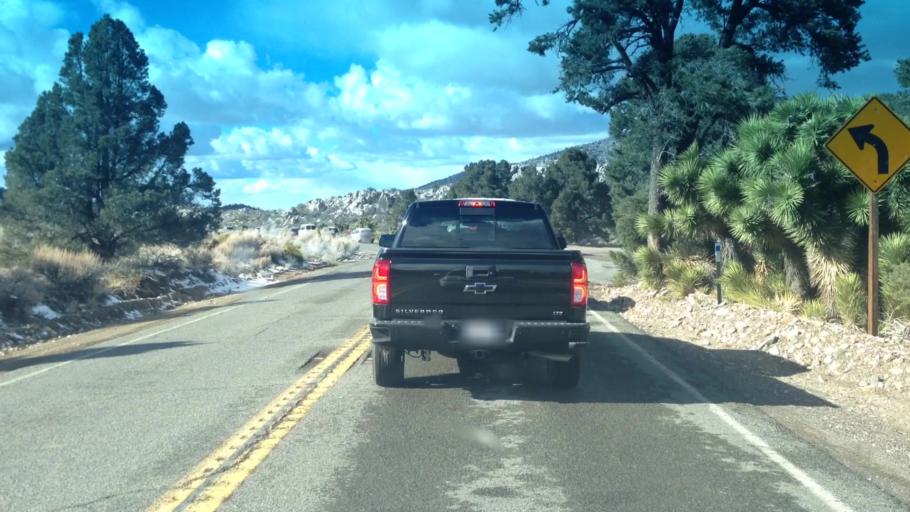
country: US
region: California
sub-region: San Bernardino County
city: Big Bear City
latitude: 34.3144
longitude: -116.8102
